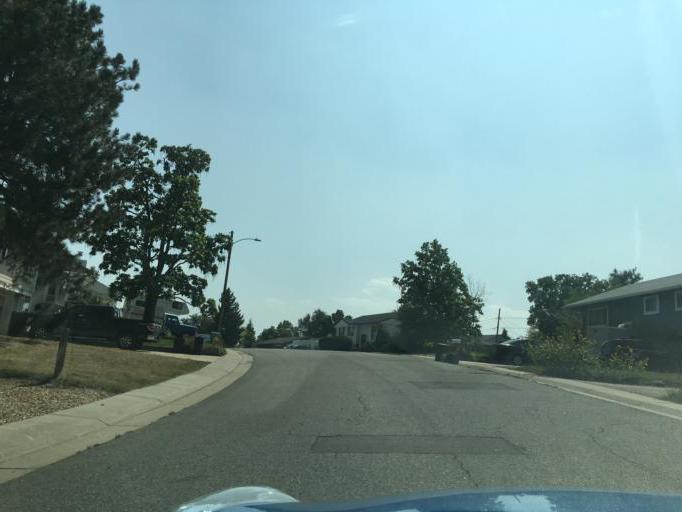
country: US
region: Colorado
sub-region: Jefferson County
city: Arvada
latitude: 39.8376
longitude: -105.0746
